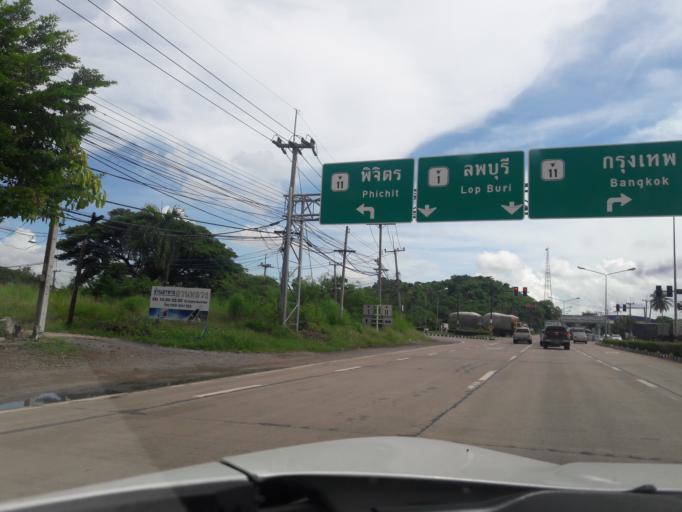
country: TH
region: Nakhon Sawan
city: Tak Fa
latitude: 15.3514
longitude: 100.5023
